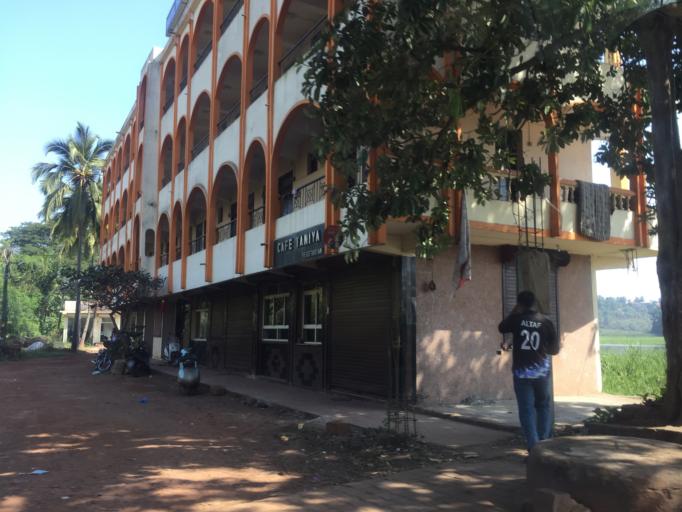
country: IN
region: Goa
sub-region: South Goa
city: Vasco Da Gama
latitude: 15.3980
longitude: 73.8179
